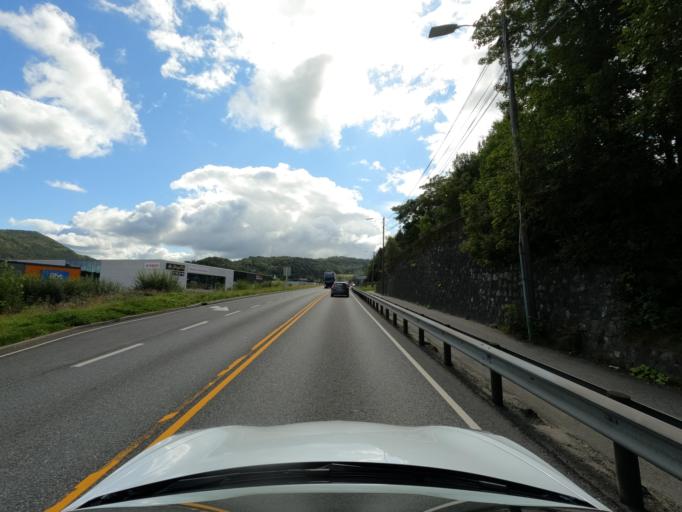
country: NO
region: Hordaland
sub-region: Bergen
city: Hylkje
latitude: 60.4879
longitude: 5.3766
